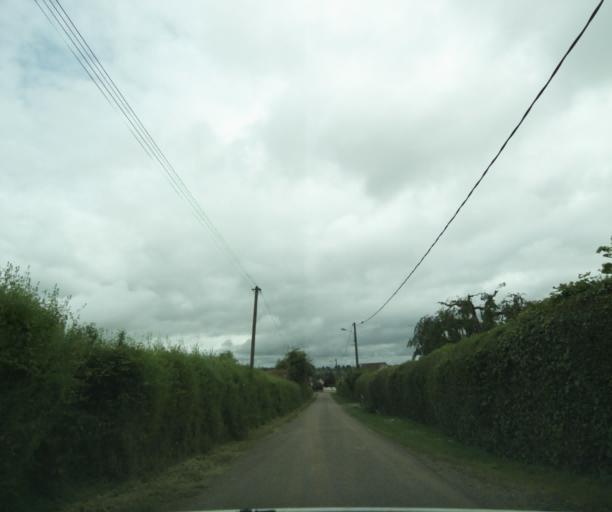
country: FR
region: Bourgogne
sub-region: Departement de Saone-et-Loire
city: Charolles
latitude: 46.4343
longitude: 4.2631
